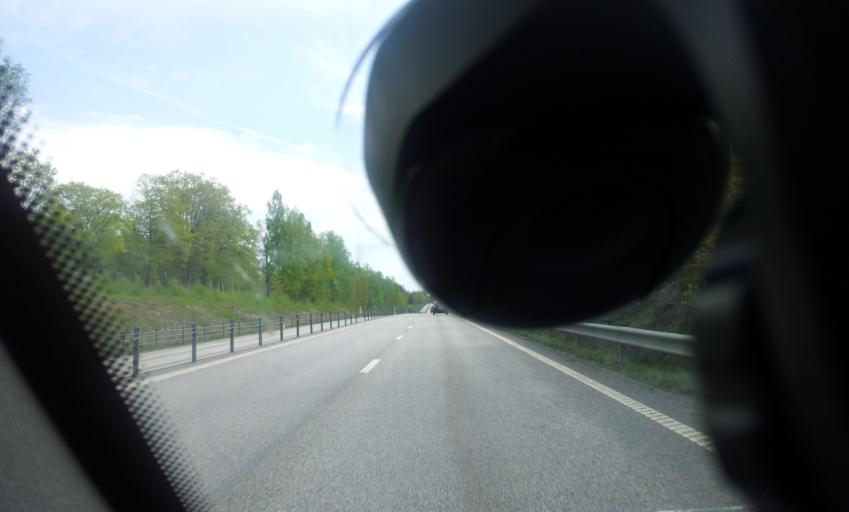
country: SE
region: Kalmar
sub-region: Vasterviks Kommun
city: Vaestervik
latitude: 57.7919
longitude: 16.5226
